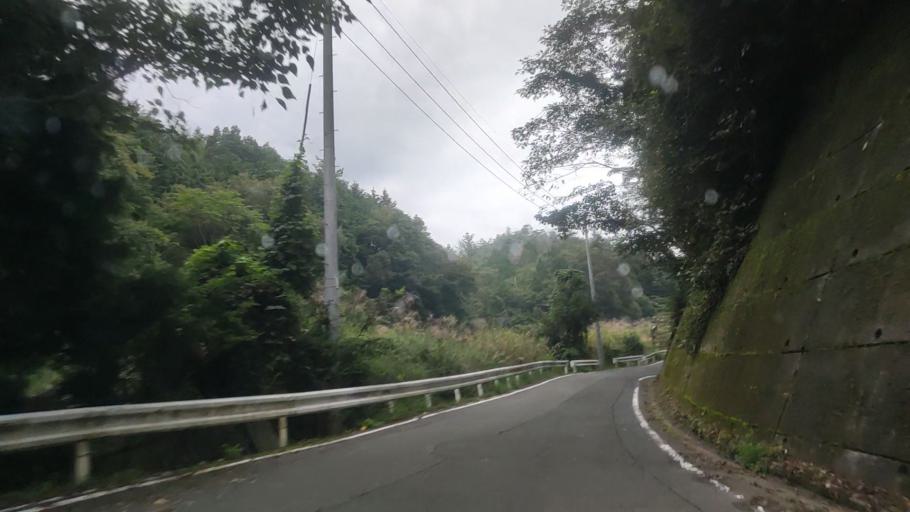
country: JP
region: Wakayama
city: Hashimoto
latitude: 34.2899
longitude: 135.6267
